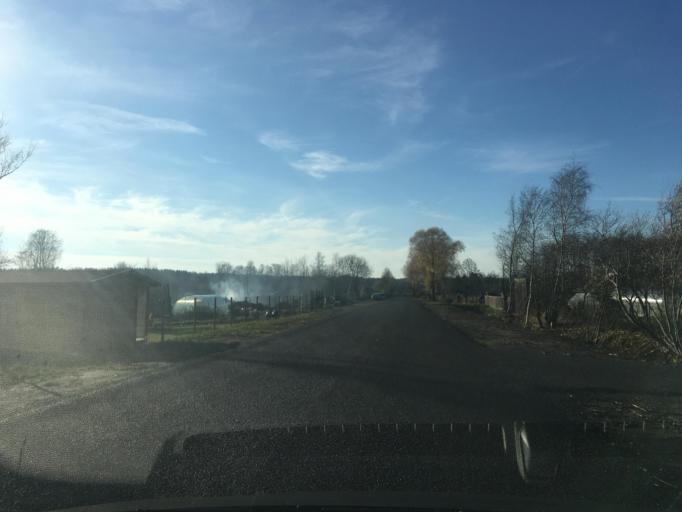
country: EE
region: Harju
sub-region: Maardu linn
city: Maardu
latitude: 59.4768
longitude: 25.0429
